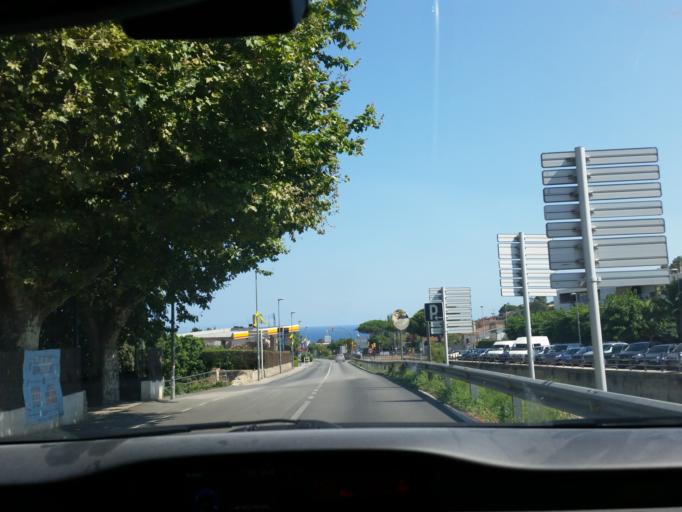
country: ES
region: Catalonia
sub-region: Provincia de Barcelona
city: Cabrils
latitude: 41.5258
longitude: 2.3659
